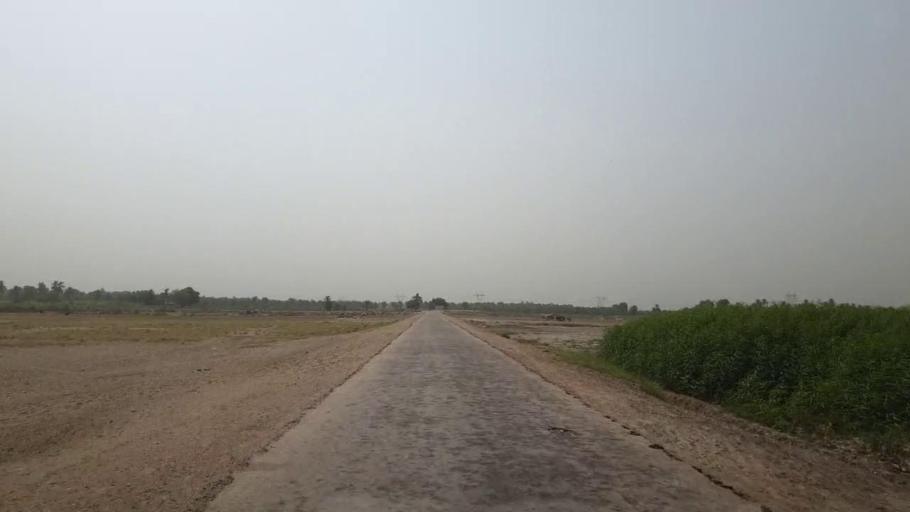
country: PK
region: Sindh
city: Gambat
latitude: 27.4228
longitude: 68.5442
